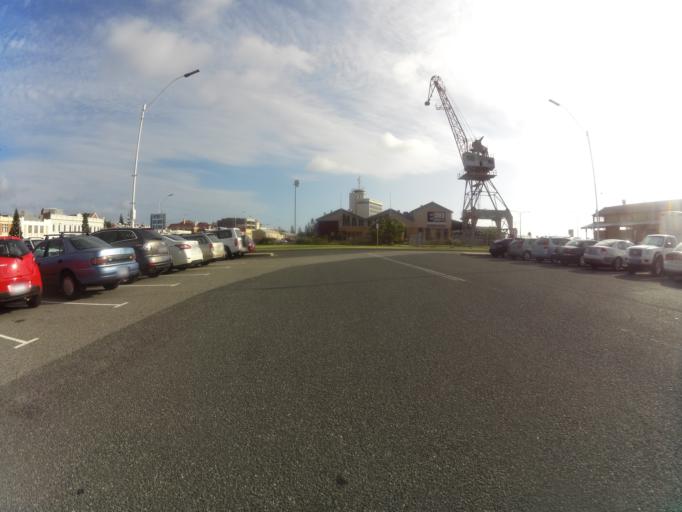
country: AU
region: Western Australia
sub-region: Fremantle
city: South Fremantle
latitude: -32.0525
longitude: 115.7437
